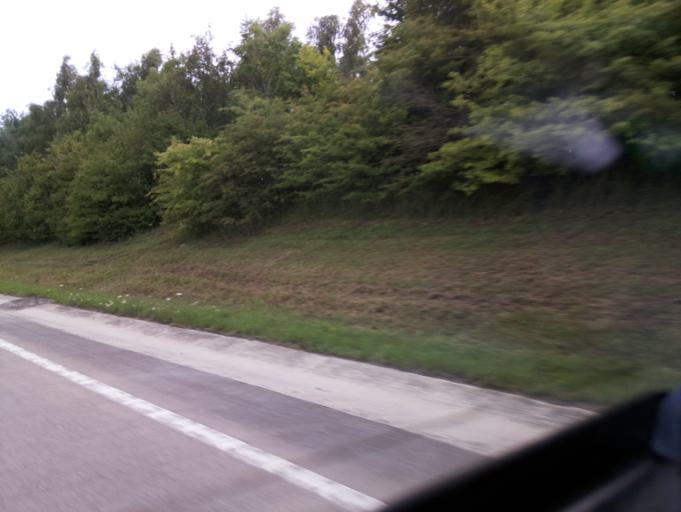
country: GB
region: England
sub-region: Gloucestershire
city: Cirencester
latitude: 51.6947
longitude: -1.9160
